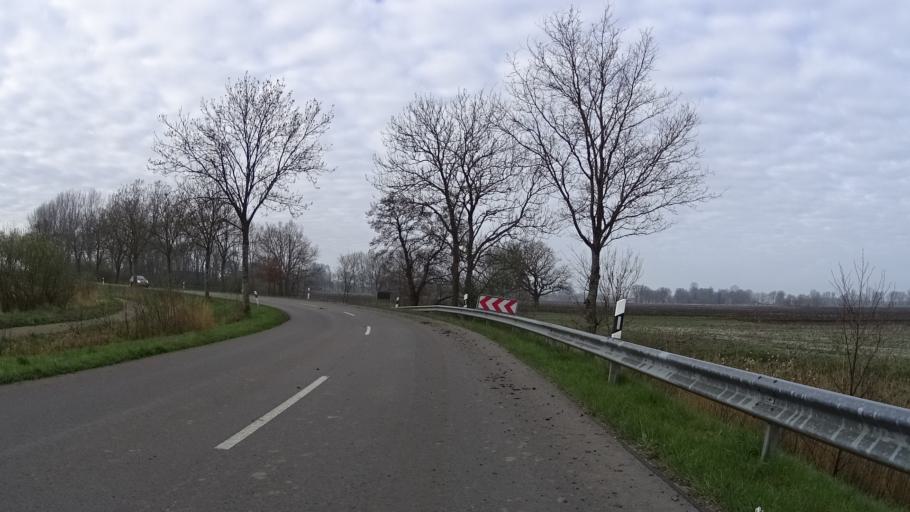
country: DE
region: Lower Saxony
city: Upgant-Schott
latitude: 53.4452
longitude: 7.3308
